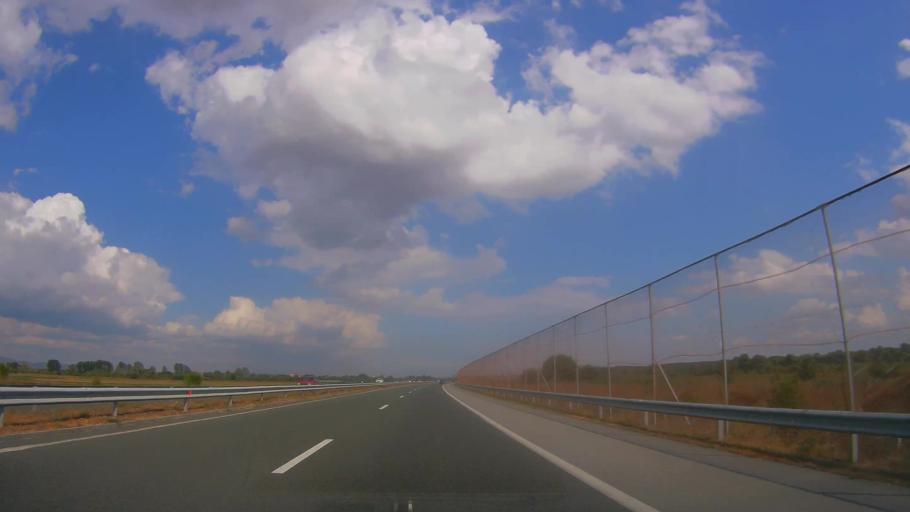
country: BG
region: Yambol
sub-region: Obshtina Yambol
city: Yambol
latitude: 42.5544
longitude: 26.5099
